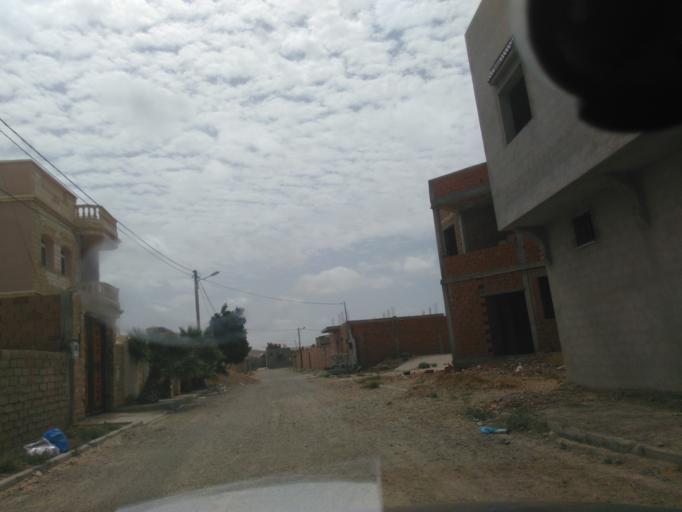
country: TN
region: Tataouine
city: Tataouine
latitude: 32.9475
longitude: 10.4703
